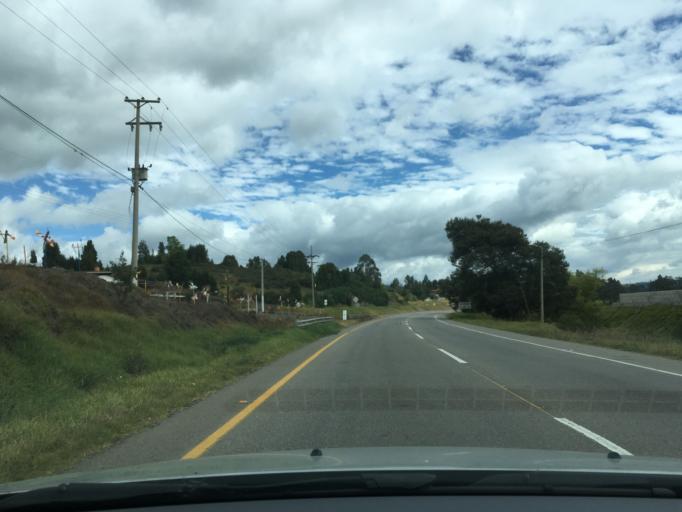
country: CO
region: Boyaca
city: Tuta
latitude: 5.7281
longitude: -73.2211
